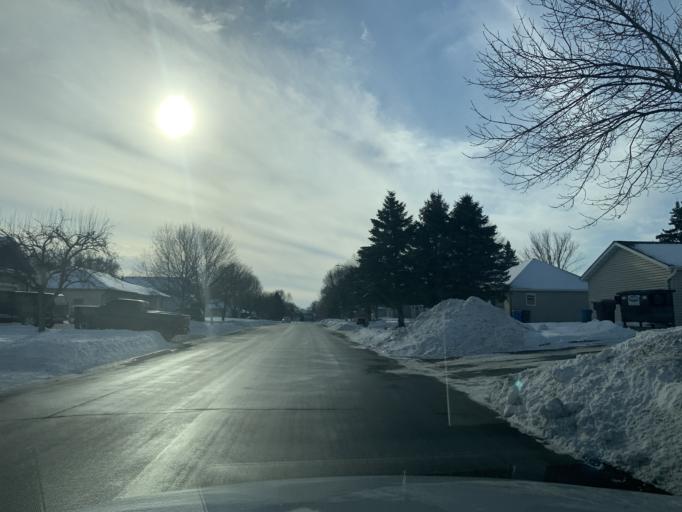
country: US
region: Minnesota
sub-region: Wright County
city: Saint Michael
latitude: 45.2086
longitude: -93.6552
